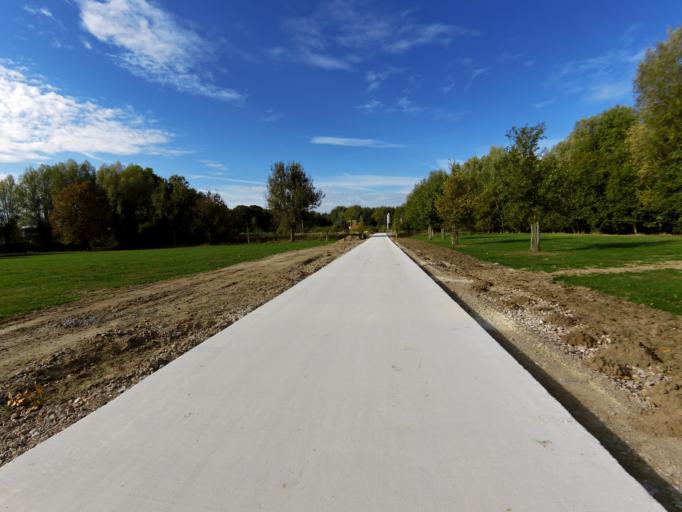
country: NL
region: Limburg
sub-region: Gemeente Onderbanken
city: Schinveld
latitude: 50.9636
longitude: 5.9756
